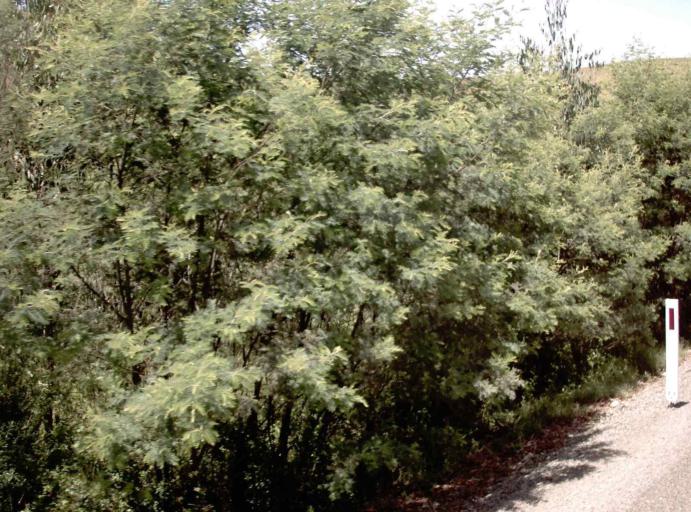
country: AU
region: Victoria
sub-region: East Gippsland
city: Bairnsdale
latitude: -37.4942
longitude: 147.8337
